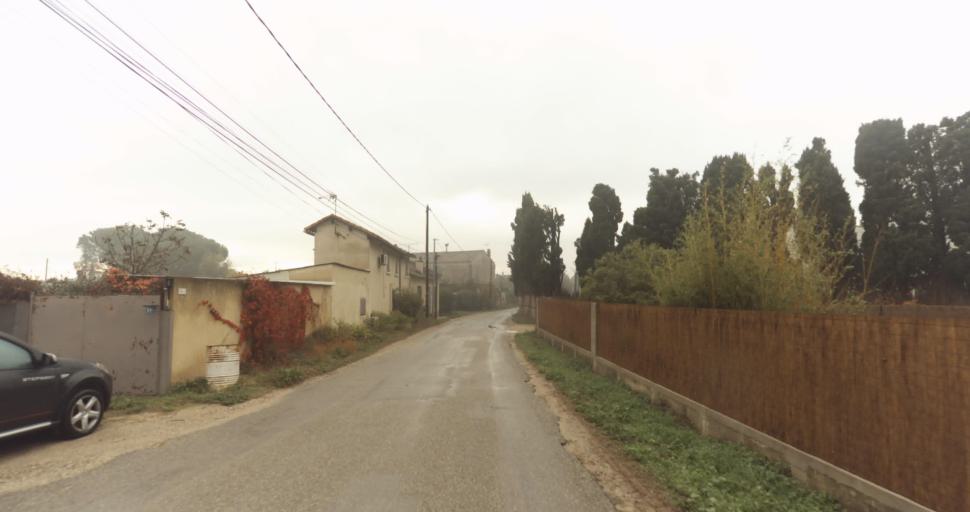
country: FR
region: Provence-Alpes-Cote d'Azur
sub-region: Departement des Bouches-du-Rhone
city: Rognonas
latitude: 43.8893
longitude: 4.8110
